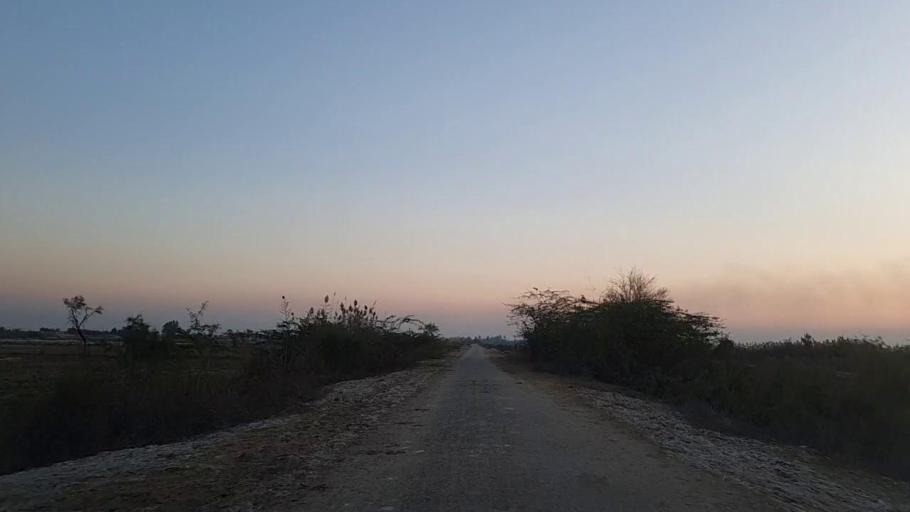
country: PK
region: Sindh
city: Bandhi
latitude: 26.5943
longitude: 68.3360
